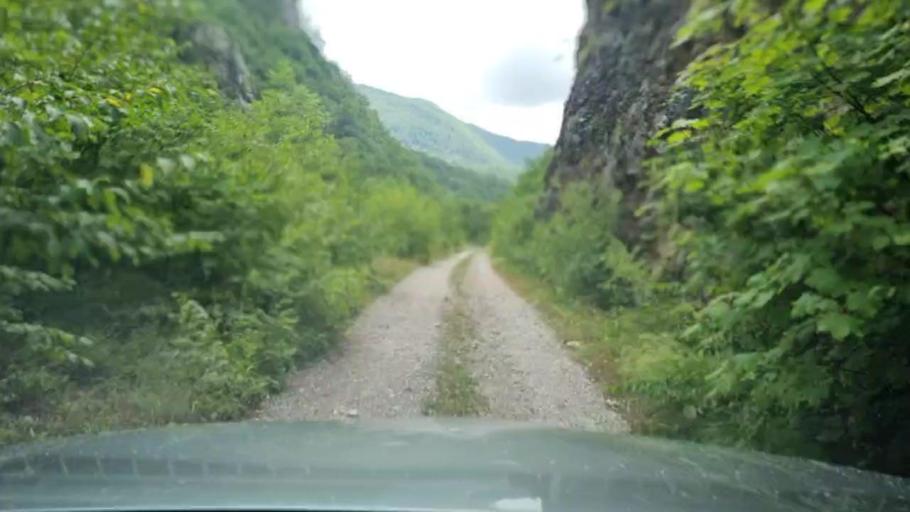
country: BA
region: Republika Srpska
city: Rogatica
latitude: 43.7657
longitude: 18.8724
